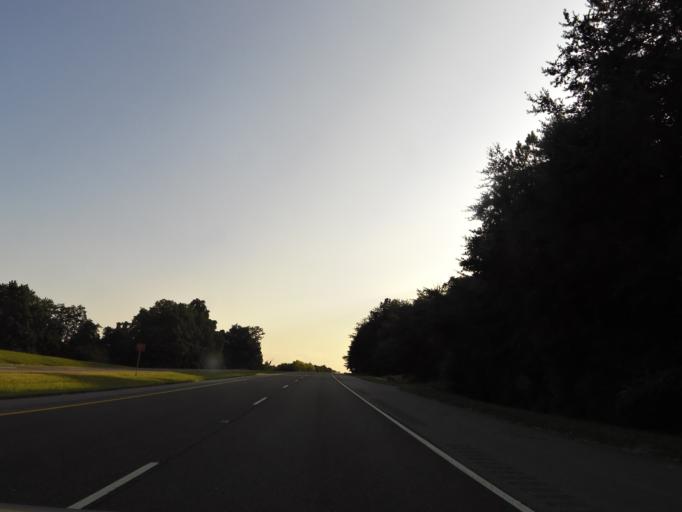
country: US
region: Tennessee
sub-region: Knox County
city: Mascot
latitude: 36.0693
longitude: -83.7756
